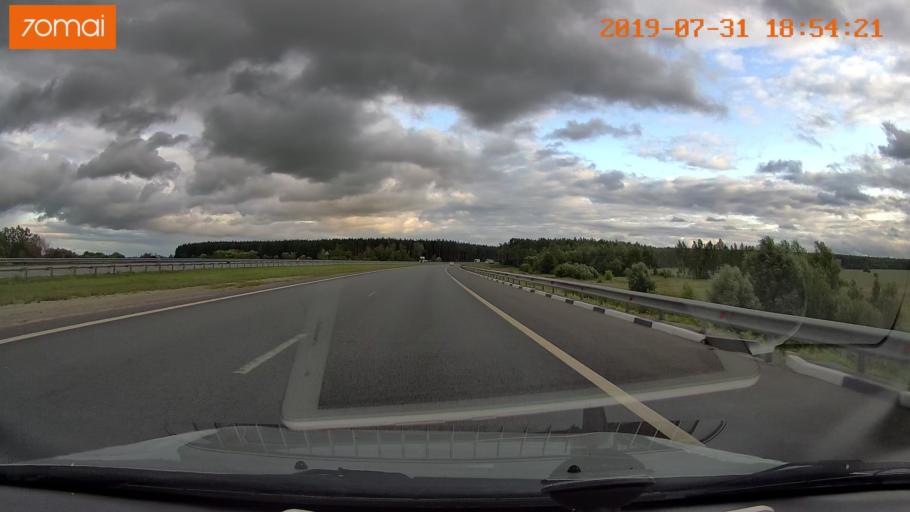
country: RU
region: Moskovskaya
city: Raduzhnyy
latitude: 55.1914
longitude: 38.6678
